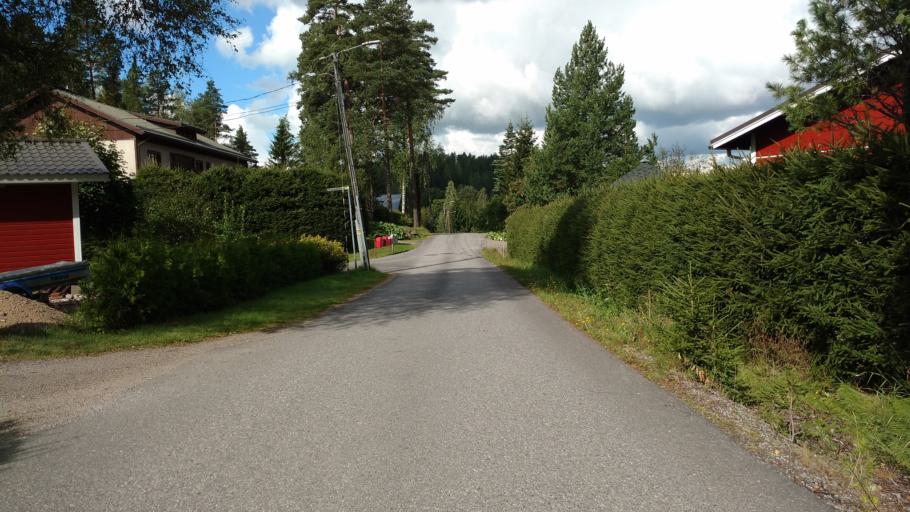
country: FI
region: Varsinais-Suomi
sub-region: Salo
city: Salo
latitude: 60.3643
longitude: 23.1825
